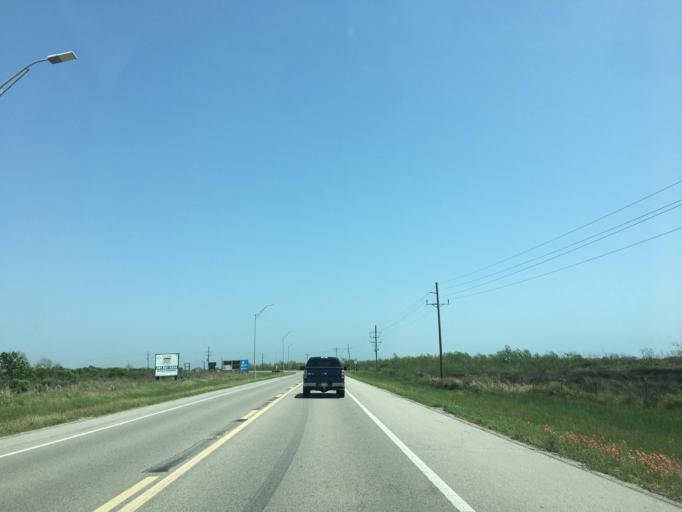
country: US
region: Texas
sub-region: Galveston County
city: Galveston
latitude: 29.3907
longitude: -94.7329
